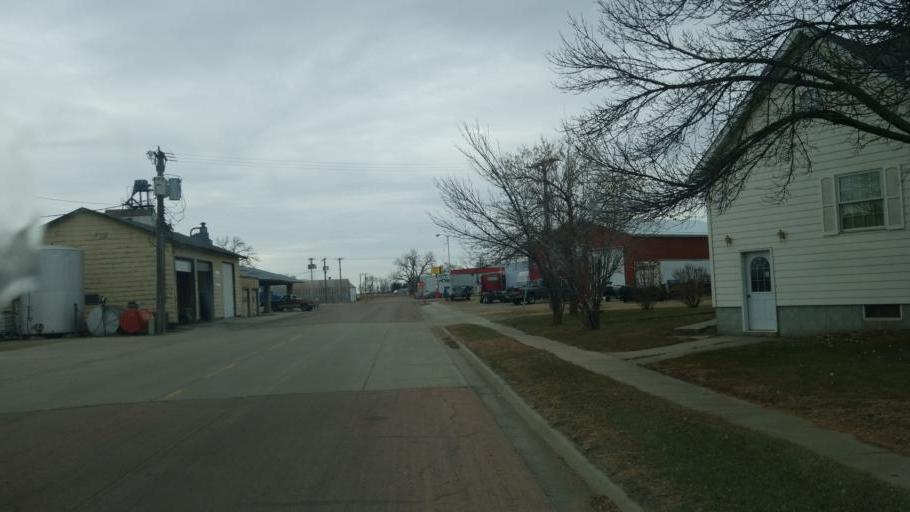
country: US
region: South Dakota
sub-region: Hutchinson County
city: Parkston
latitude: 43.2232
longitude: -97.9645
